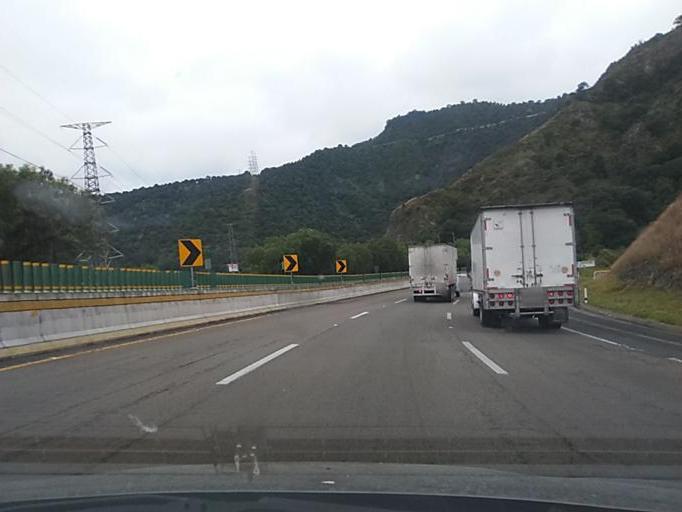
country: MX
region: Mexico City
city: Xochimilco
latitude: 19.2296
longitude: -99.1432
